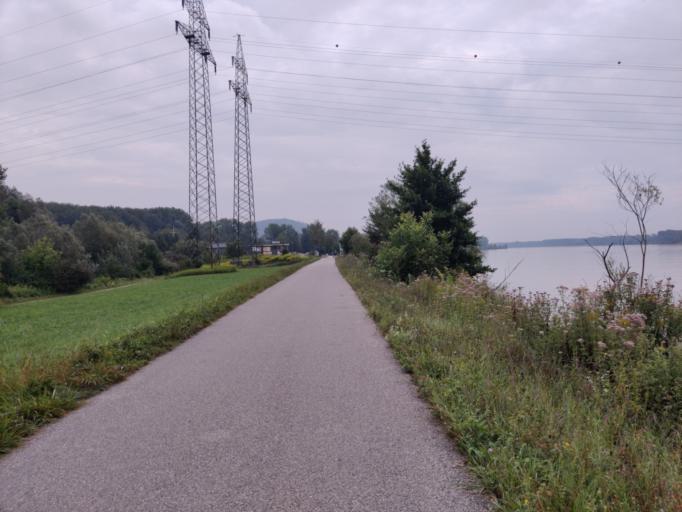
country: AT
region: Upper Austria
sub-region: Politischer Bezirk Urfahr-Umgebung
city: Steyregg
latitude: 48.2709
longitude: 14.3798
